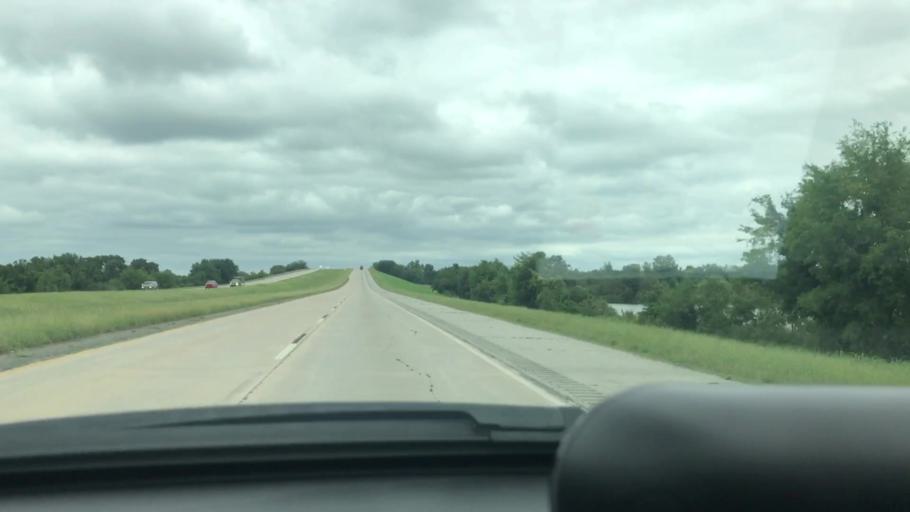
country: US
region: Oklahoma
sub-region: Wagoner County
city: Wagoner
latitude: 35.8781
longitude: -95.4028
